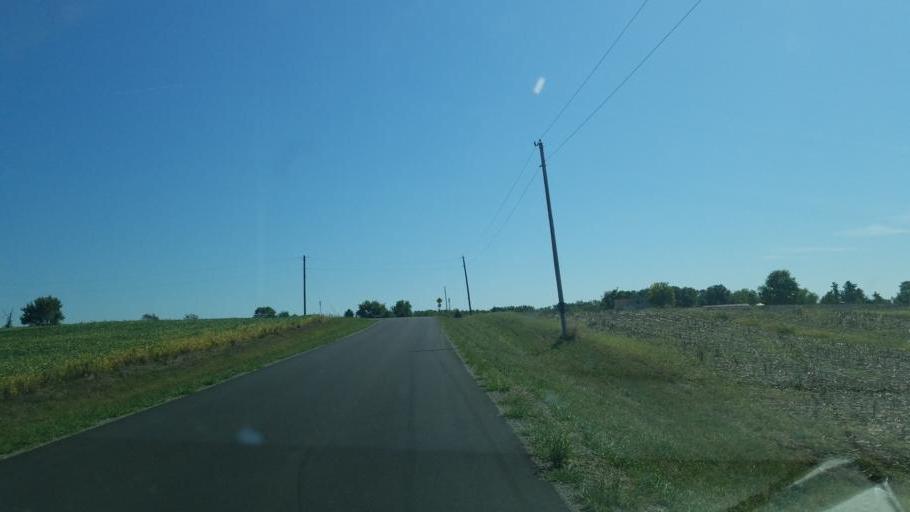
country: US
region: Ohio
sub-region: Logan County
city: Bellefontaine
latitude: 40.4059
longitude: -83.7702
